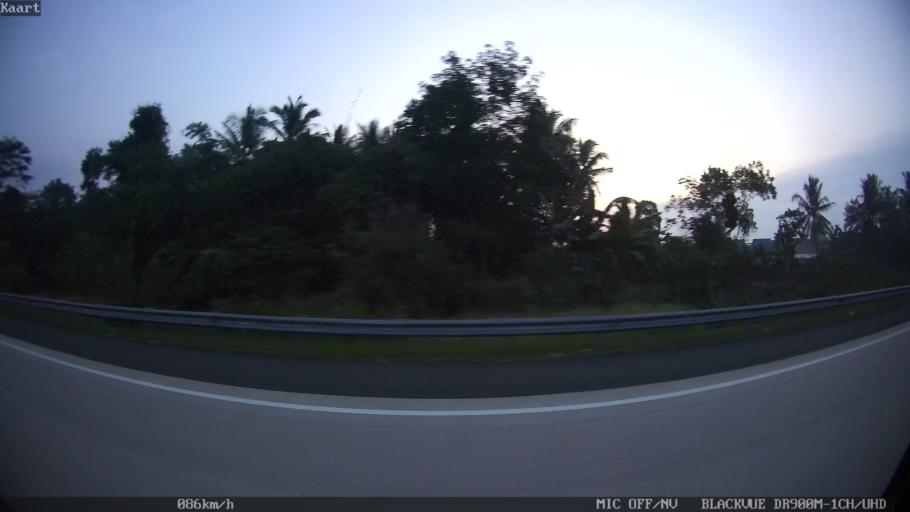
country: ID
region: Lampung
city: Sidorejo
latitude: -5.6353
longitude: 105.5690
